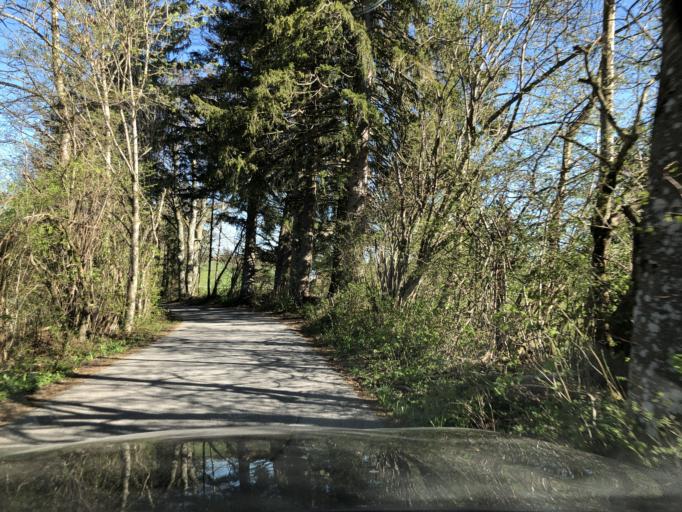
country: DE
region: Bavaria
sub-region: Swabia
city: Ruckholz
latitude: 47.6608
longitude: 10.5333
